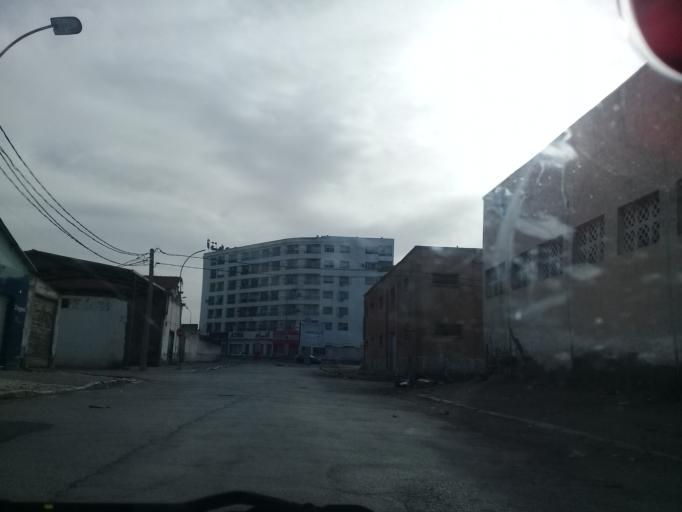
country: TN
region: Tunis
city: Tunis
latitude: 36.7910
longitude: 10.1851
